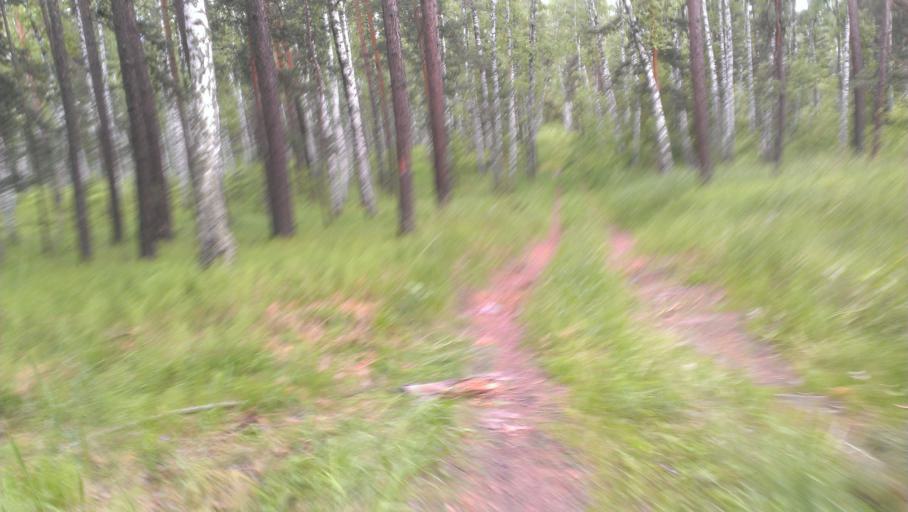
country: RU
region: Altai Krai
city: Sannikovo
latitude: 53.3405
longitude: 84.0480
